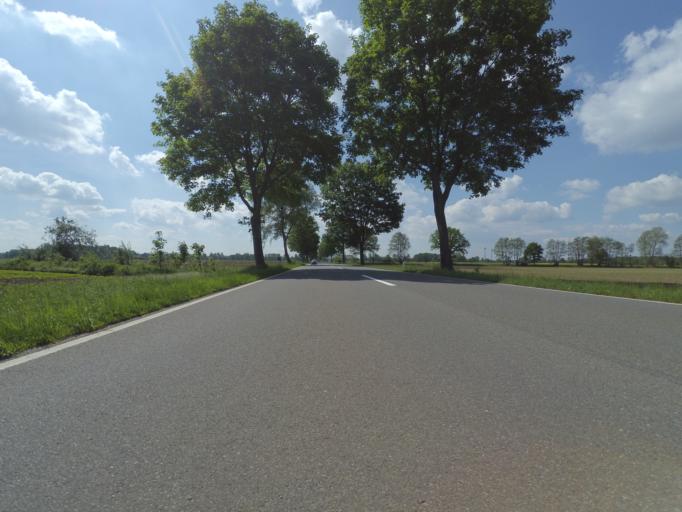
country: DE
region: Lower Saxony
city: Langlingen
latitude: 52.5248
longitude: 10.2608
